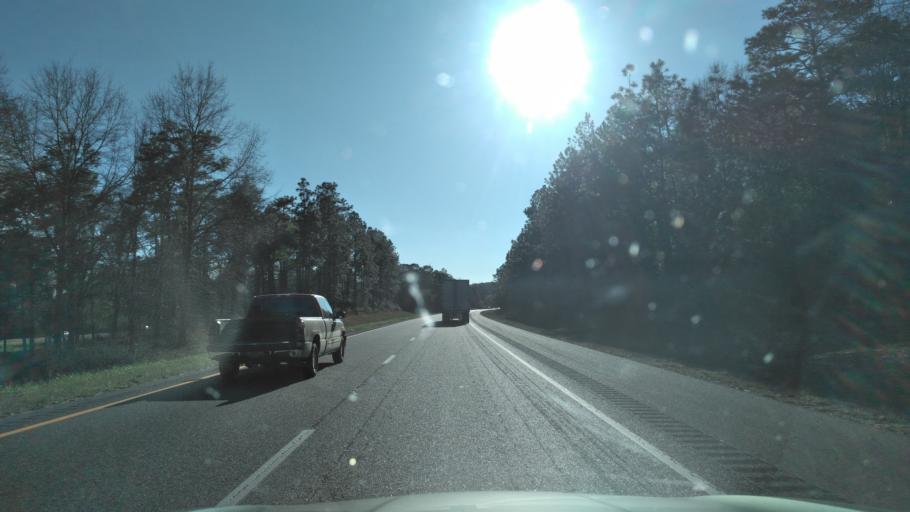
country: US
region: Alabama
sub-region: Escambia County
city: Atmore
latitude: 31.0671
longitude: -87.5597
